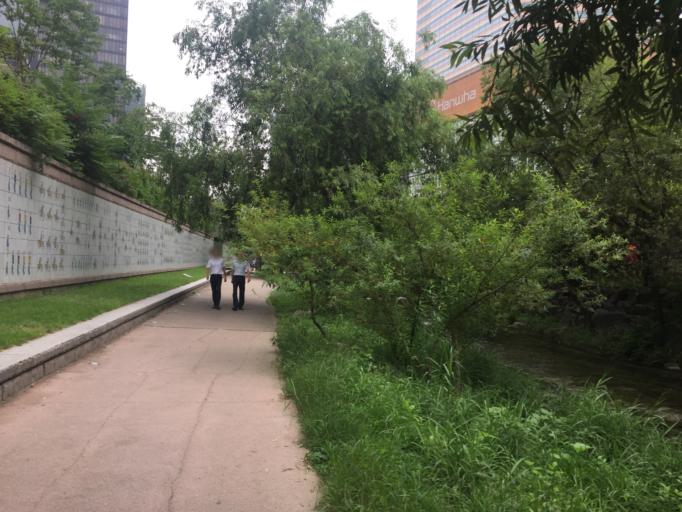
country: KR
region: Seoul
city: Seoul
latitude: 37.5685
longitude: 126.9849
